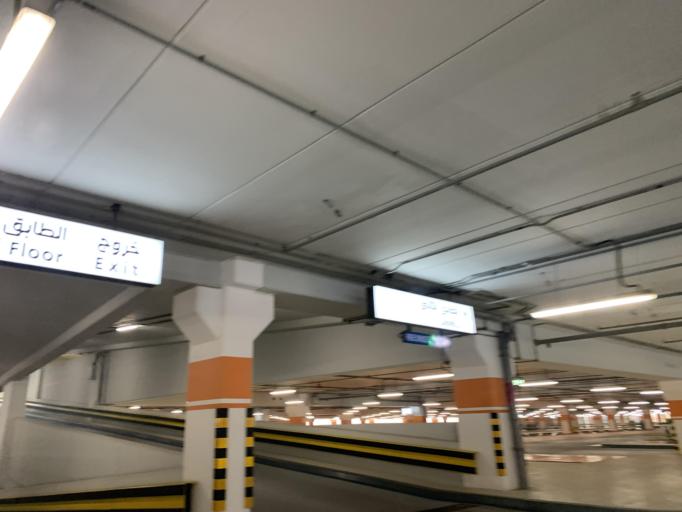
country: BH
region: Muharraq
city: Al Muharraq
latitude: 26.2676
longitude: 50.6291
